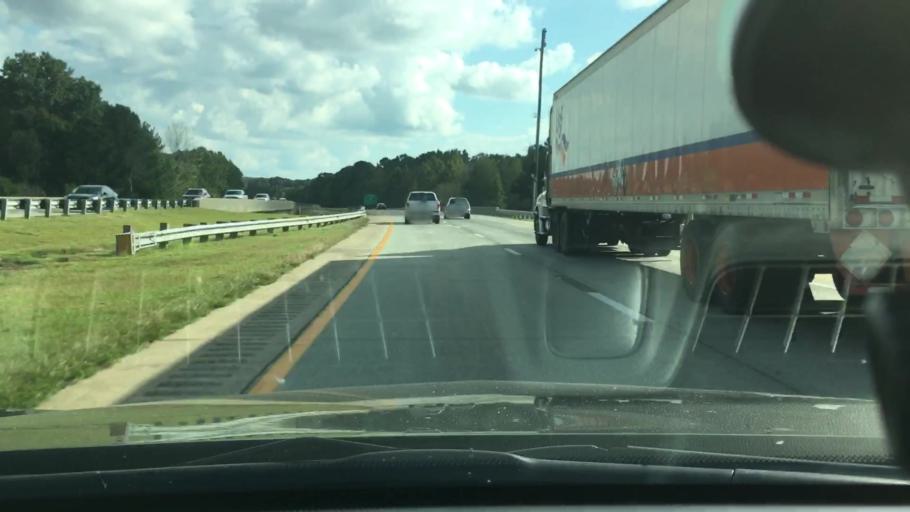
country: US
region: North Carolina
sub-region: Orange County
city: Chapel Hill
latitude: 35.9877
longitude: -79.0754
